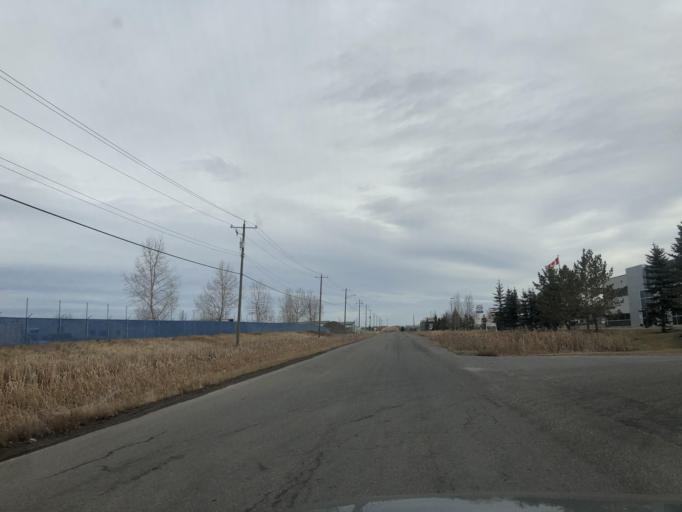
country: CA
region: Alberta
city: Chestermere
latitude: 50.9833
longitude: -113.9090
